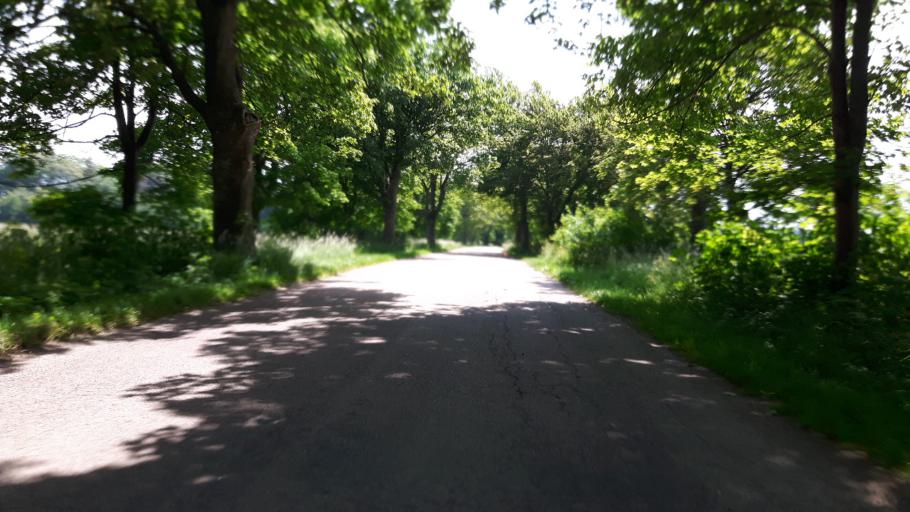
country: PL
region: Pomeranian Voivodeship
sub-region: Powiat wejherowski
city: Choczewo
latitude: 54.7426
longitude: 17.8124
